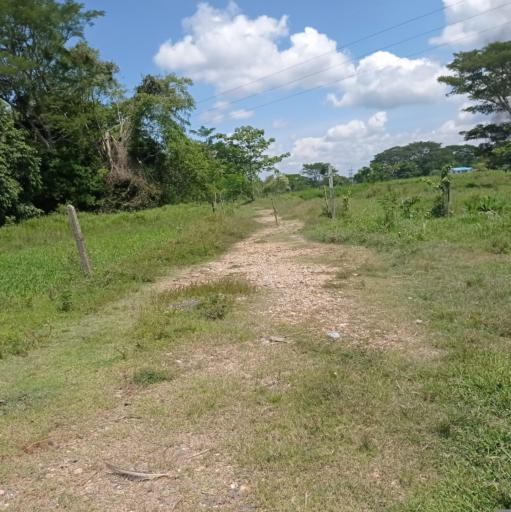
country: CO
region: Santander
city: Barrancabermeja
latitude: 7.0942
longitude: -73.8766
